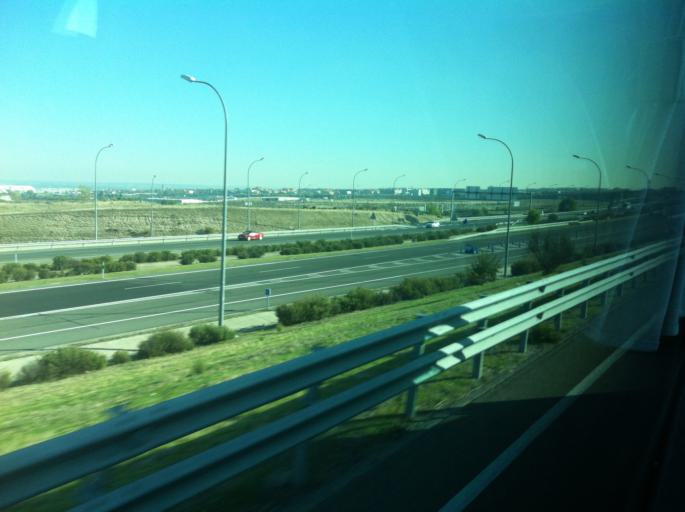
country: ES
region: Madrid
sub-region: Provincia de Madrid
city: Barajas de Madrid
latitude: 40.4911
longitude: -3.6024
